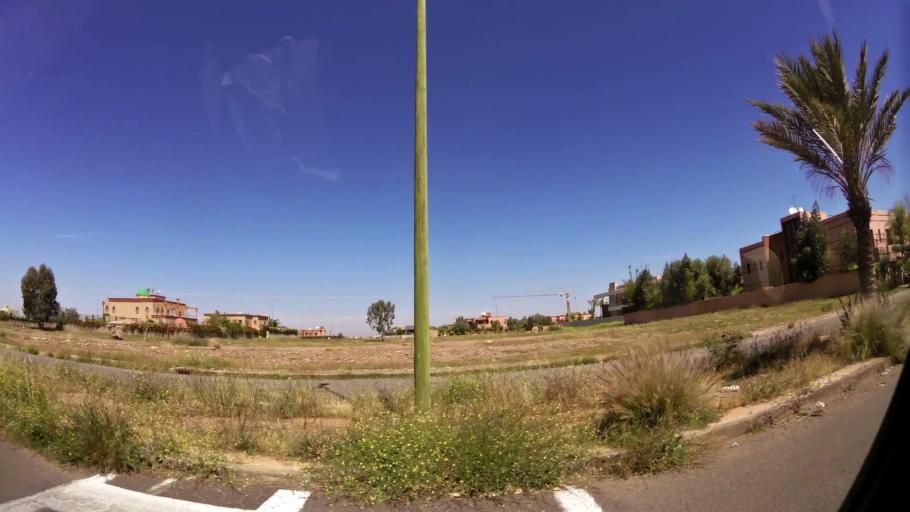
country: MA
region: Marrakech-Tensift-Al Haouz
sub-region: Marrakech
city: Marrakesh
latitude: 31.5879
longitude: -7.9970
